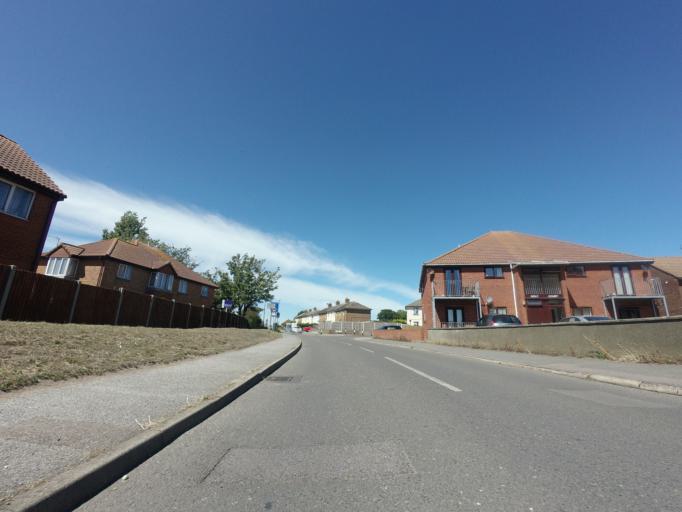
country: GB
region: England
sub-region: Kent
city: Deal
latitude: 51.2360
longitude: 1.3987
